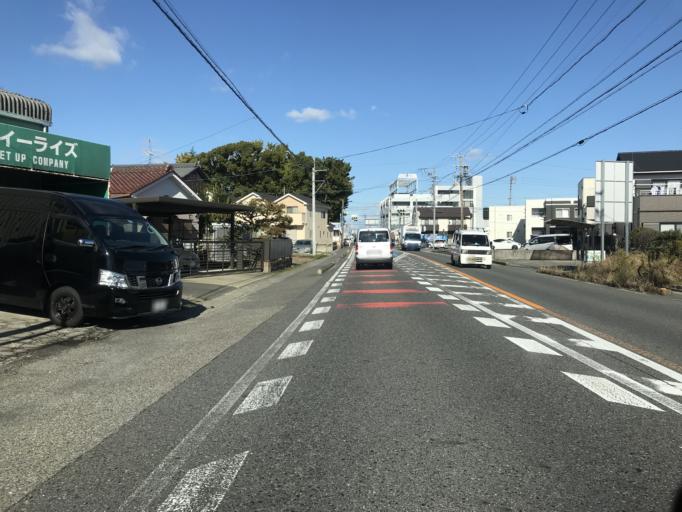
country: JP
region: Aichi
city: Inazawa
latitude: 35.2270
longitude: 136.8395
